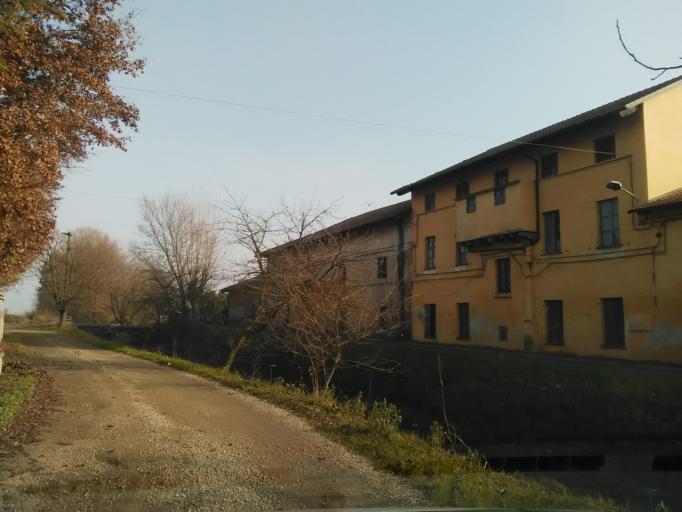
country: IT
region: Piedmont
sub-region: Provincia di Vercelli
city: Lamporo
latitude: 45.2477
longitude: 8.0746
